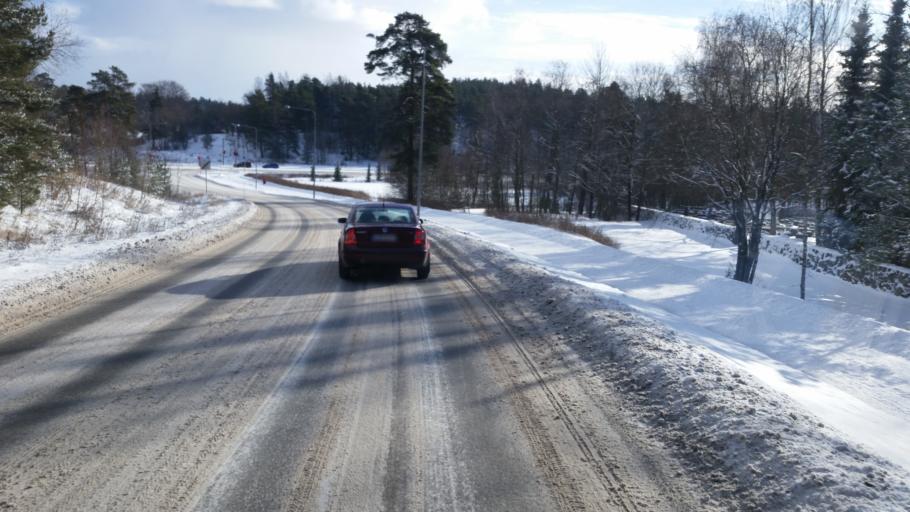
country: FI
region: Varsinais-Suomi
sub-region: Turku
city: Turku
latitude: 60.4348
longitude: 22.3142
